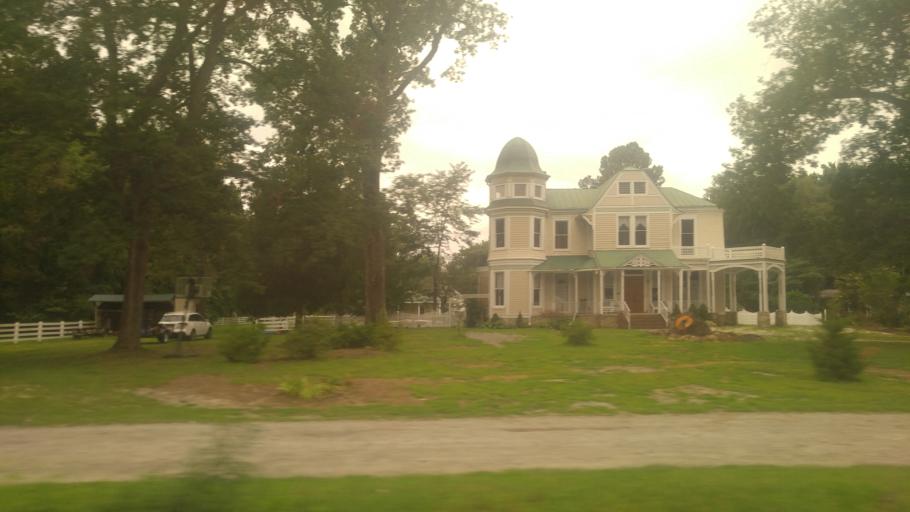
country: US
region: Virginia
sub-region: Hanover County
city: Ashland
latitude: 37.7334
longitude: -77.4893
